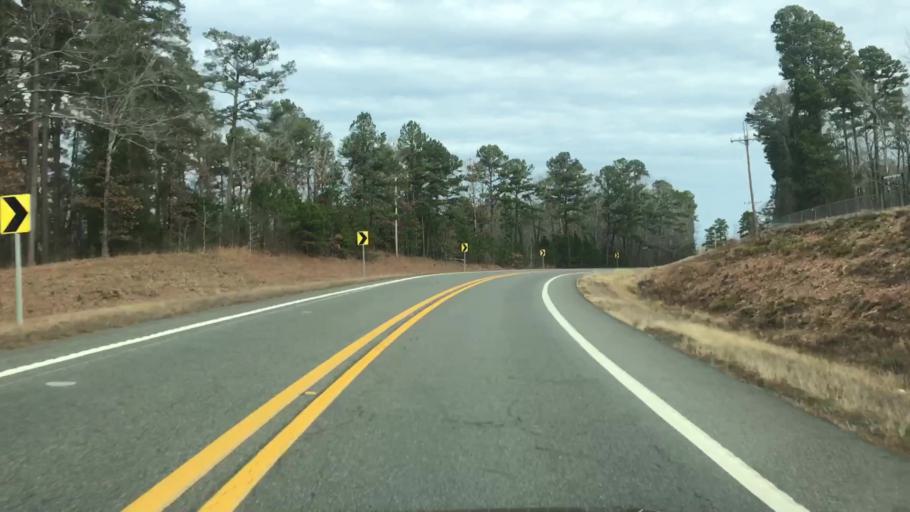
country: US
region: Arkansas
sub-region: Montgomery County
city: Mount Ida
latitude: 34.6132
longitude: -93.7033
